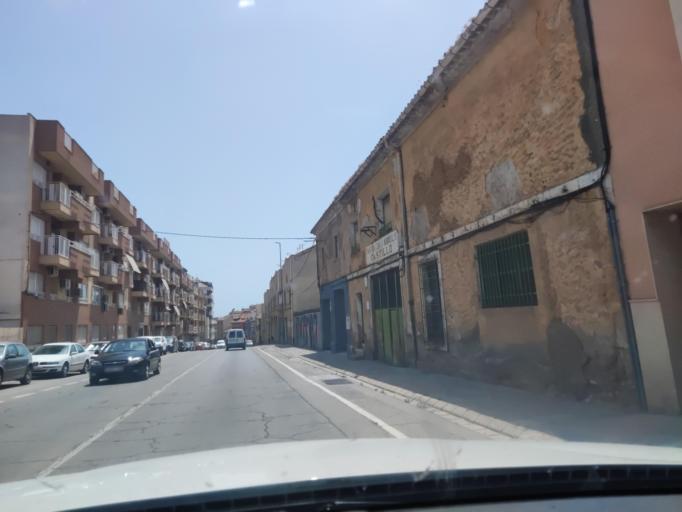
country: ES
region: Castille-La Mancha
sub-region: Provincia de Albacete
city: Hellin
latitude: 38.5146
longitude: -1.6972
